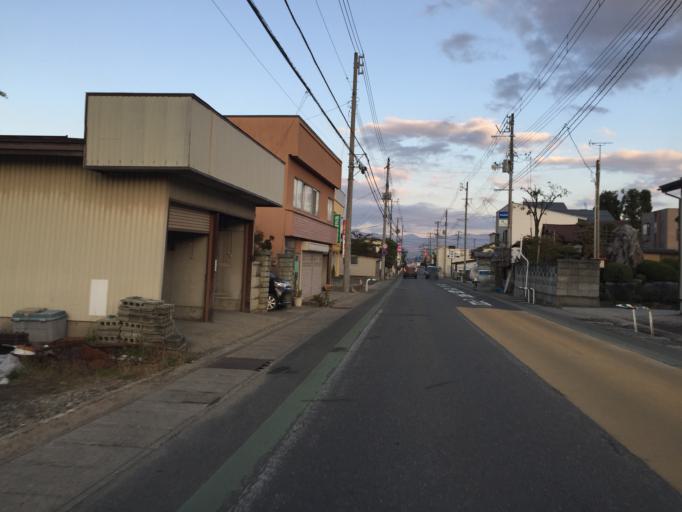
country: JP
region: Yamagata
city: Yonezawa
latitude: 37.9123
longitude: 140.0858
